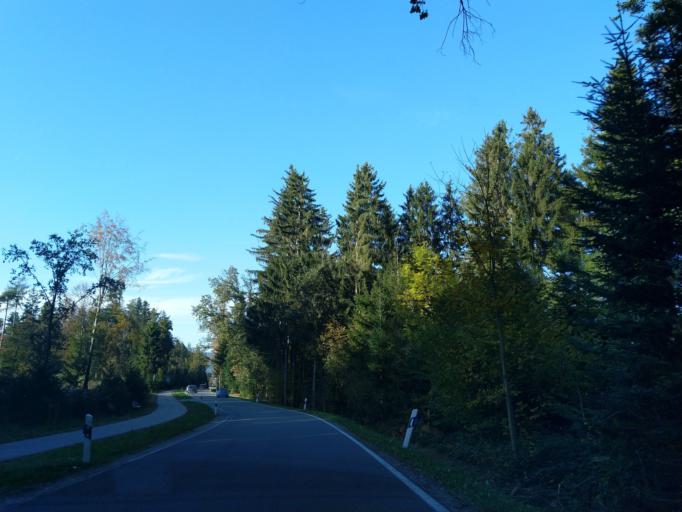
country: DE
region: Bavaria
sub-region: Lower Bavaria
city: Metten
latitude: 48.8759
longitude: 12.9011
